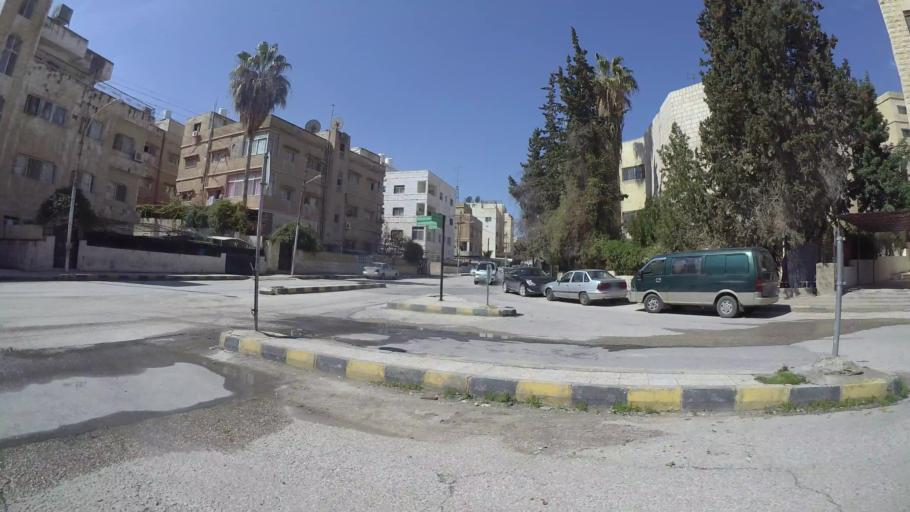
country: JO
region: Amman
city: Amman
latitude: 31.9770
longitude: 35.9903
